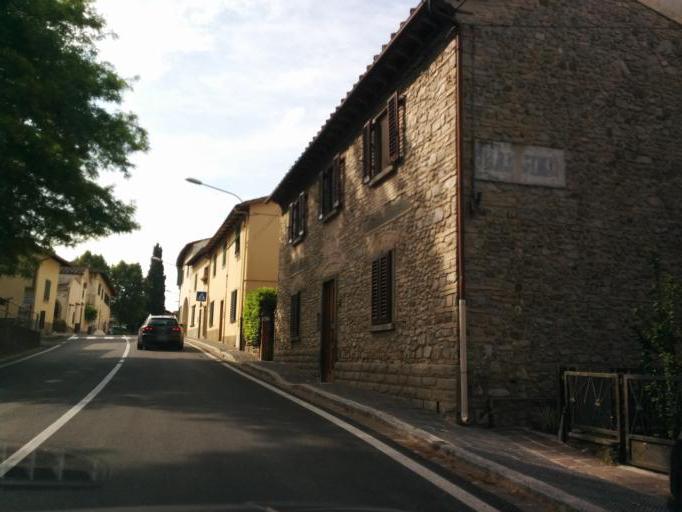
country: IT
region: Tuscany
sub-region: Province of Florence
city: San Casciano in Val di Pesa
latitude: 43.6172
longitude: 11.1894
